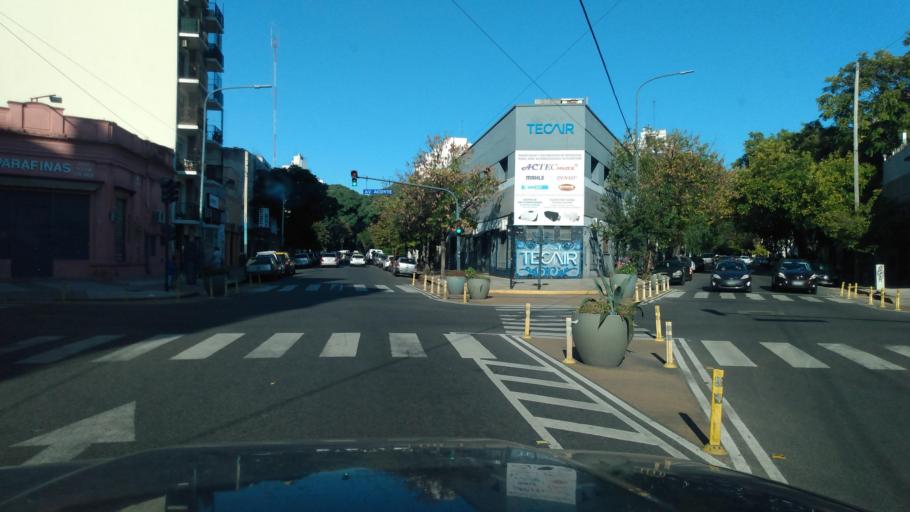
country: AR
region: Buenos Aires F.D.
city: Colegiales
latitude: -34.6013
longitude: -58.4449
